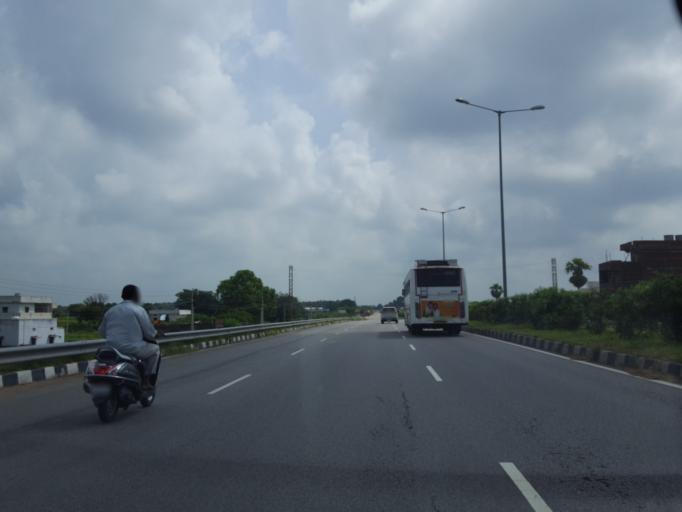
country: IN
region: Telangana
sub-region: Nalgonda
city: Nalgonda
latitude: 17.2294
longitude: 79.0214
